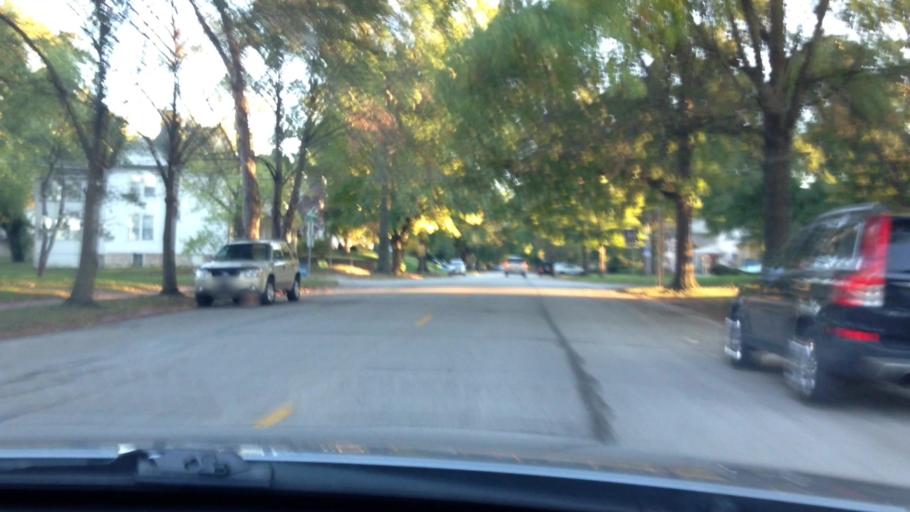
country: US
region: Kansas
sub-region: Leavenworth County
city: Leavenworth
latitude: 39.3083
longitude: -94.9207
